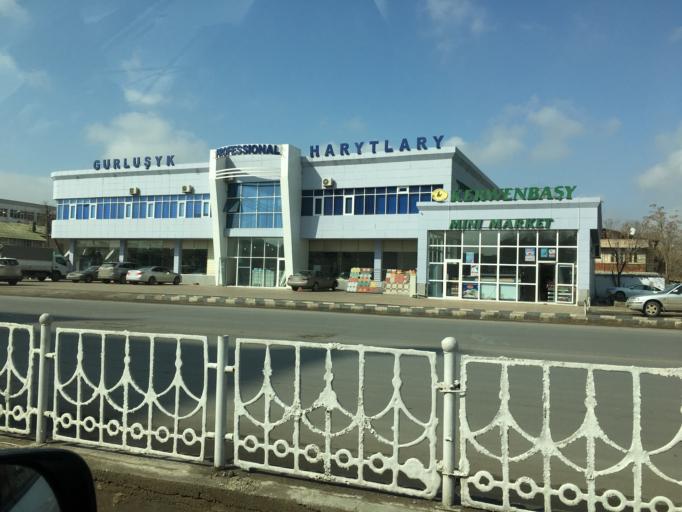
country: TM
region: Mary
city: Mary
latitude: 37.5969
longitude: 61.8300
